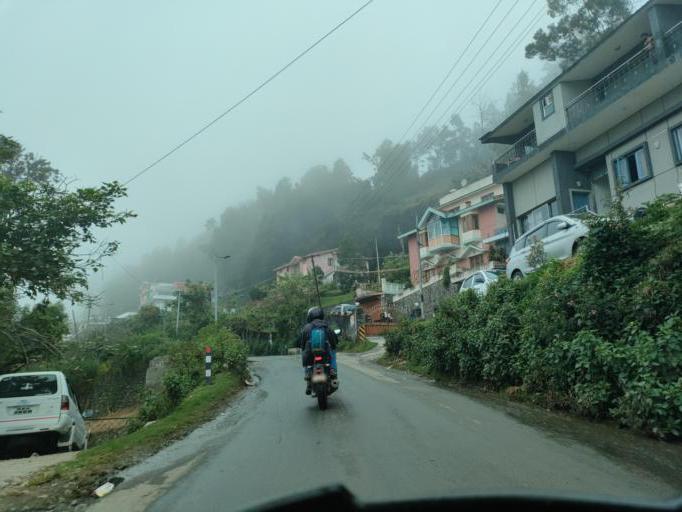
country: IN
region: Tamil Nadu
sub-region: Dindigul
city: Kodaikanal
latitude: 10.2348
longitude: 77.4783
